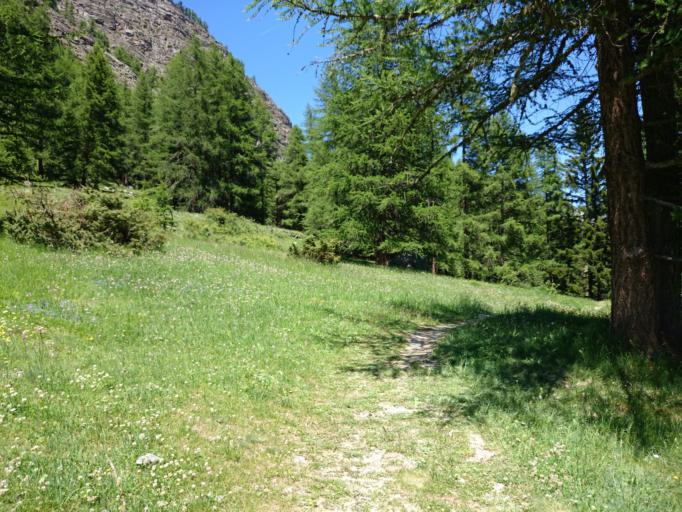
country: IT
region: Aosta Valley
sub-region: Valle d'Aosta
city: Cogne
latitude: 45.5904
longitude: 7.3421
